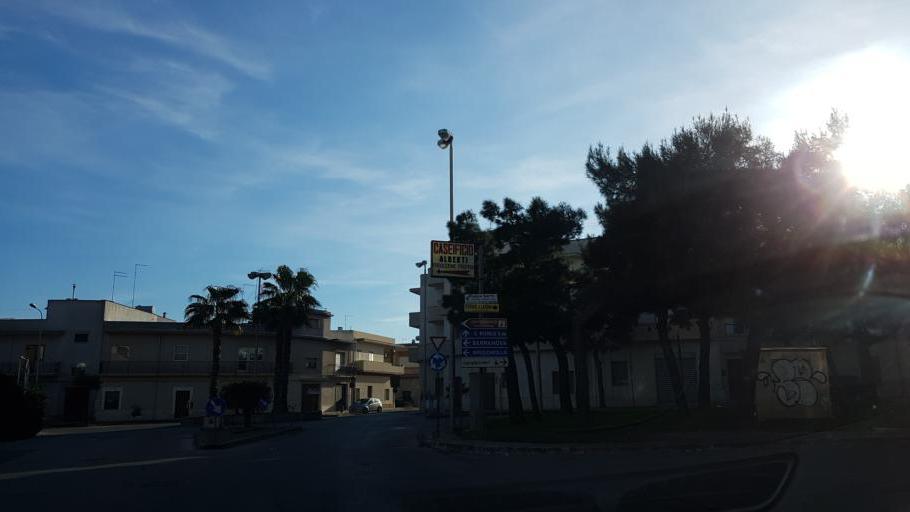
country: IT
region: Apulia
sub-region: Provincia di Brindisi
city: Carovigno
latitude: 40.7043
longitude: 17.6635
